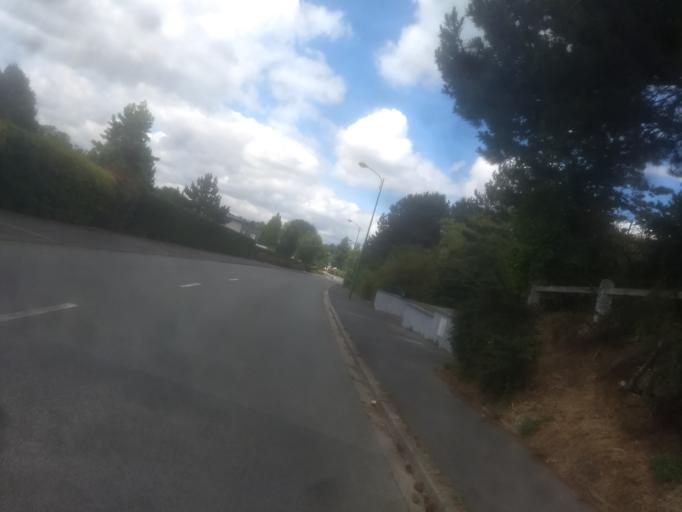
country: FR
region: Nord-Pas-de-Calais
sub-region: Departement du Pas-de-Calais
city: Anzin-Saint-Aubin
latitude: 50.3137
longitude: 2.7368
